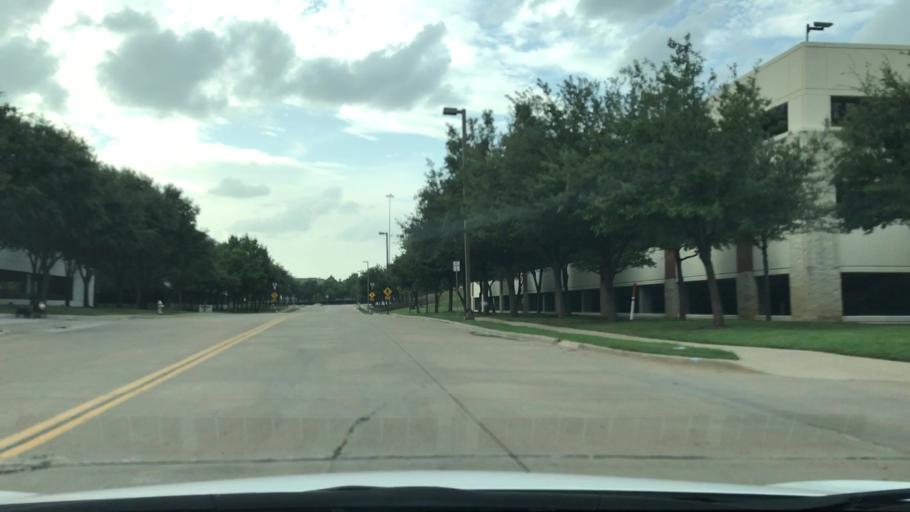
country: US
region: Texas
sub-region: Dallas County
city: Farmers Branch
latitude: 32.8979
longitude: -96.9628
